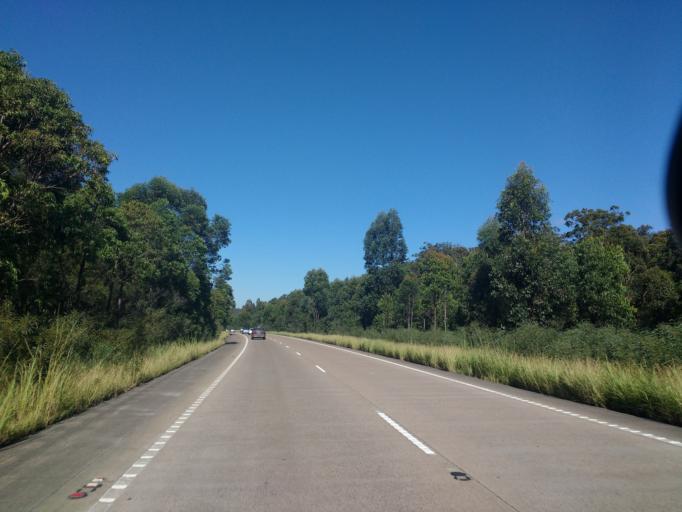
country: AU
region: New South Wales
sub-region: Lake Macquarie Shire
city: Holmesville
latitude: -32.9204
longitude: 151.5522
